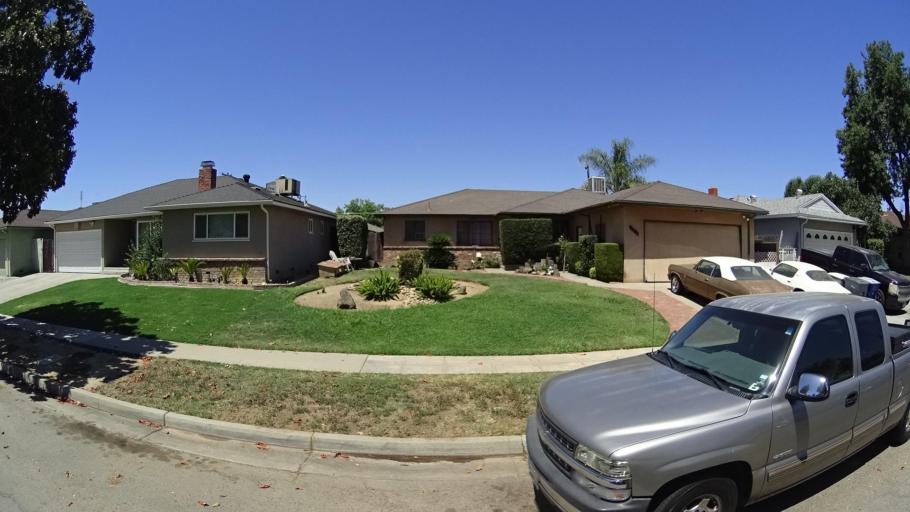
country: US
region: California
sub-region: Fresno County
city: Fresno
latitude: 36.8028
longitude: -119.7750
